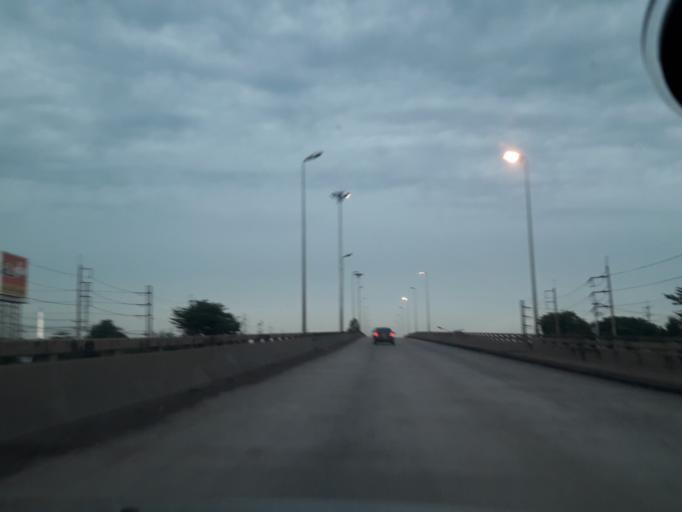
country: TH
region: Pathum Thani
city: Ban Rangsit
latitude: 14.0283
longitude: 100.7489
